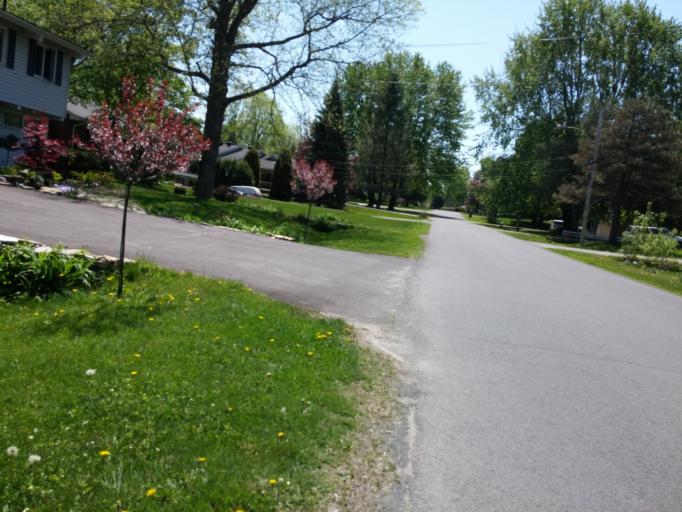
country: CA
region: Quebec
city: Baie-D'Urfe
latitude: 45.4221
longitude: -73.9000
